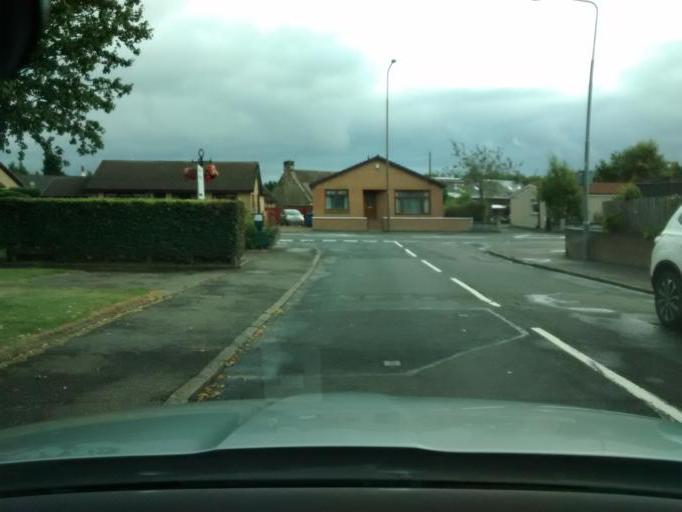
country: GB
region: Scotland
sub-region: West Lothian
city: Bathgate
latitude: 55.9011
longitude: -3.6574
